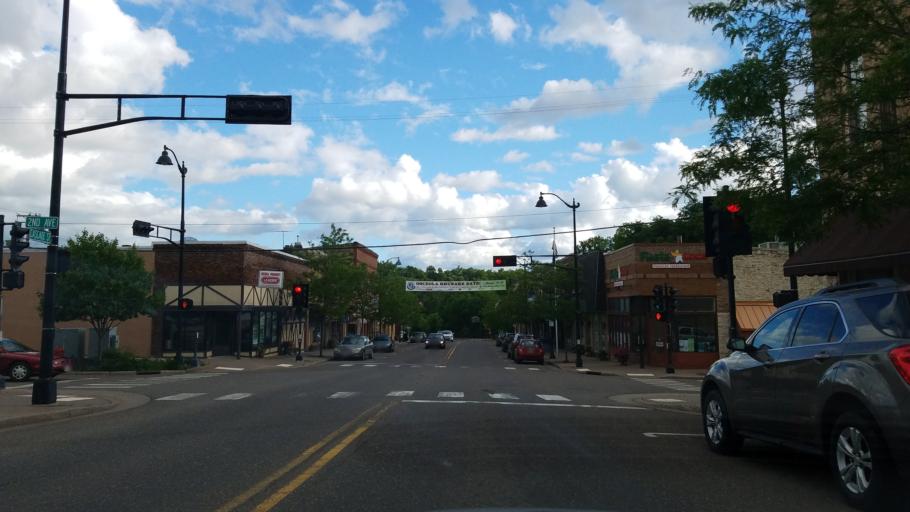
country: US
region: Wisconsin
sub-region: Polk County
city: Osceola
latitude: 45.3211
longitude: -92.7056
